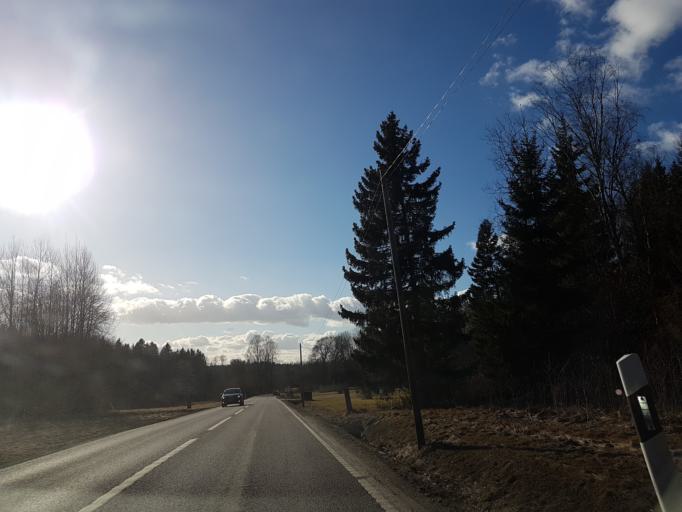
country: SE
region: Stockholm
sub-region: Norrtalje Kommun
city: Rimbo
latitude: 59.7338
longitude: 18.4372
